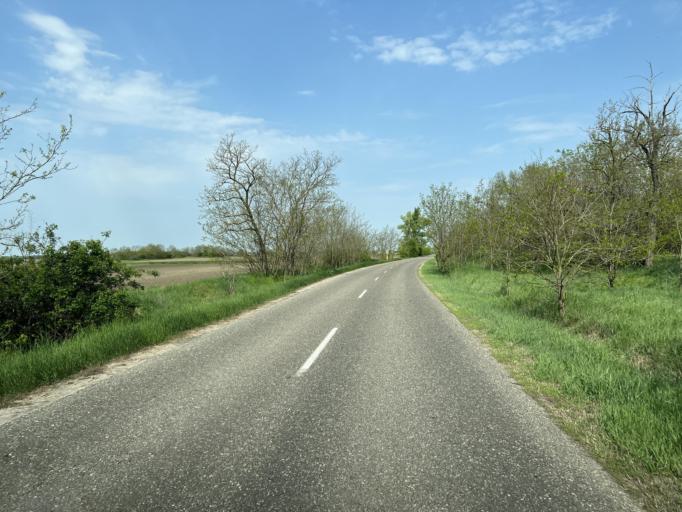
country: HU
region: Pest
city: Tortel
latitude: 47.1052
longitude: 19.9915
